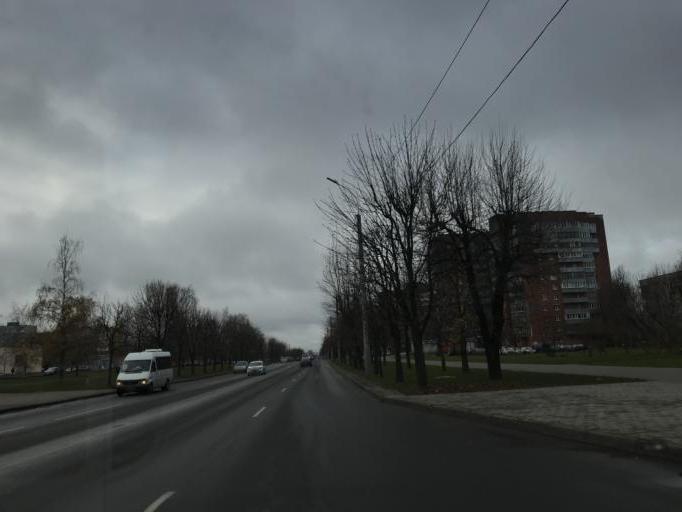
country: BY
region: Mogilev
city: Mahilyow
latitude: 53.8740
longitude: 30.3306
